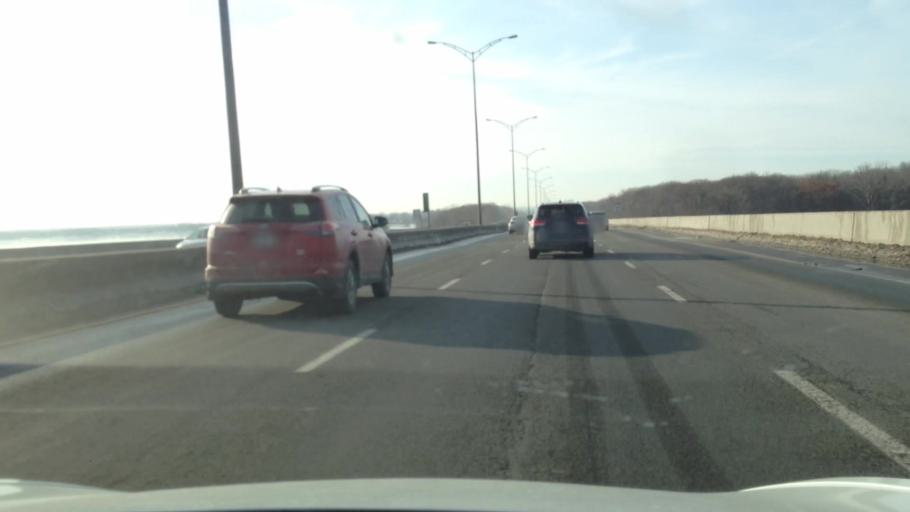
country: CA
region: Quebec
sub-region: Monteregie
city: Pincourt
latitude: 45.4204
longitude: -73.9848
